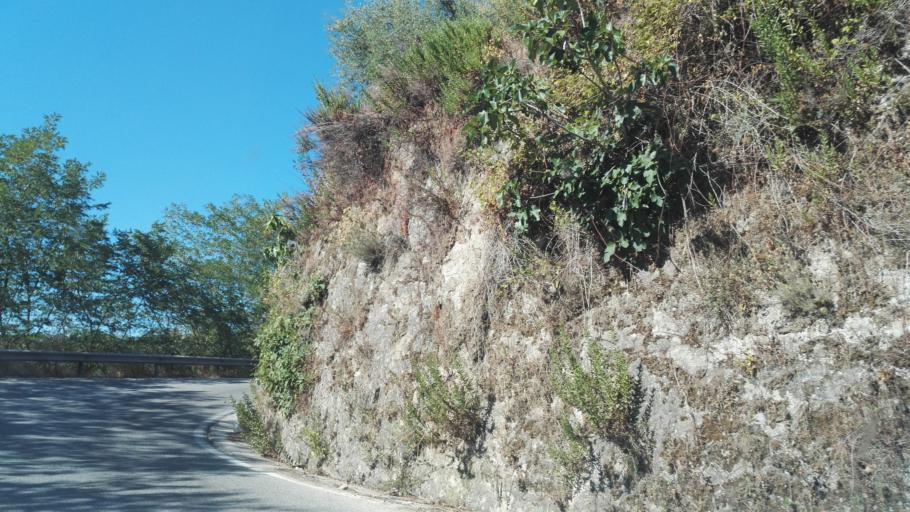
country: IT
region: Calabria
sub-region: Provincia di Vibo-Valentia
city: Sorianello
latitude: 38.5910
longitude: 16.2374
